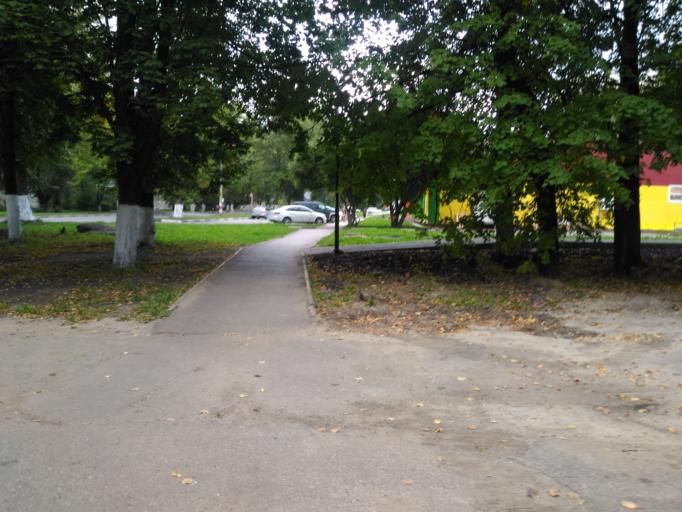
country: RU
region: Ulyanovsk
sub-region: Ulyanovskiy Rayon
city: Ulyanovsk
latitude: 54.2634
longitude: 48.3283
